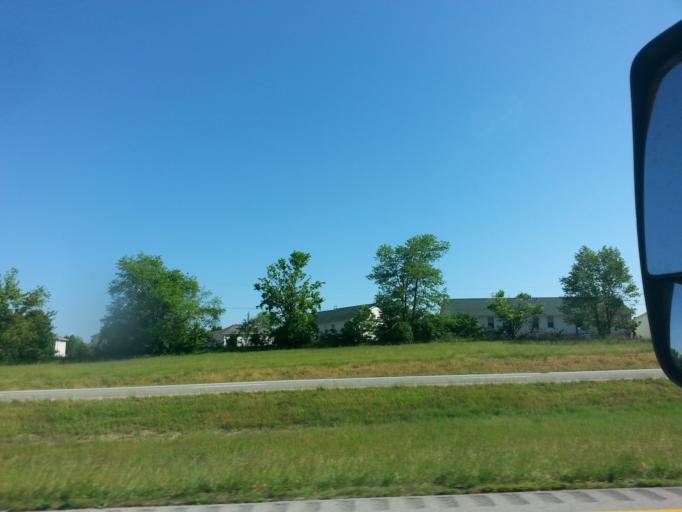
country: US
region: Kentucky
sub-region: Shelby County
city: Shelbyville
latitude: 38.1844
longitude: -85.2053
